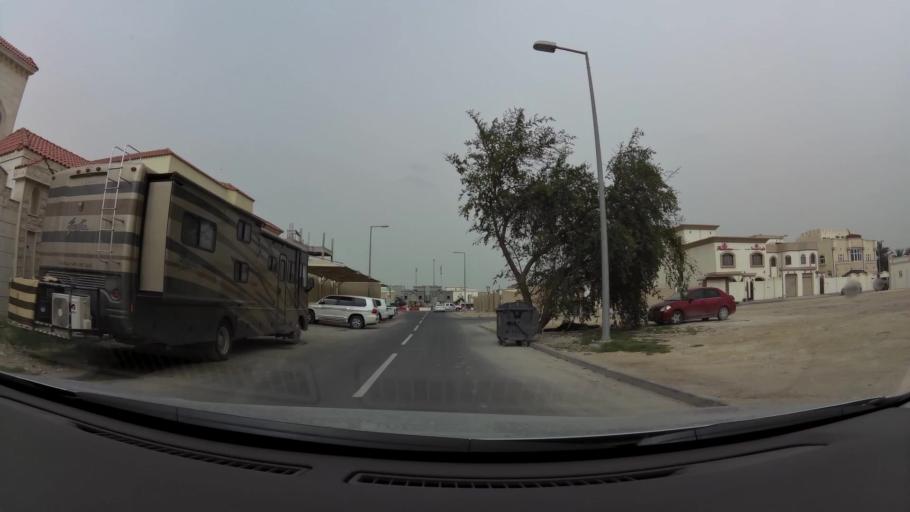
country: QA
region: Baladiyat ad Dawhah
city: Doha
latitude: 25.2459
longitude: 51.5158
